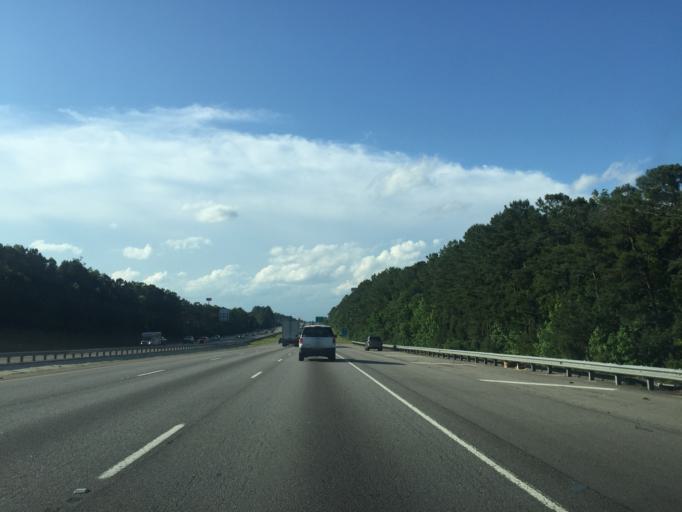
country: US
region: Georgia
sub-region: Chatham County
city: Pooler
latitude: 32.1032
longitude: -81.2369
